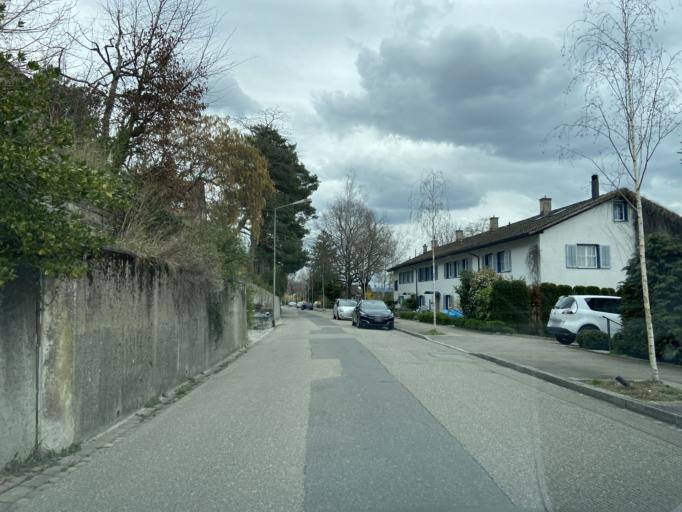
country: CH
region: Zurich
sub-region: Bezirk Winterthur
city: Wuelflingen (Kreis 6) / Lindenplatz
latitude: 47.5118
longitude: 8.7038
